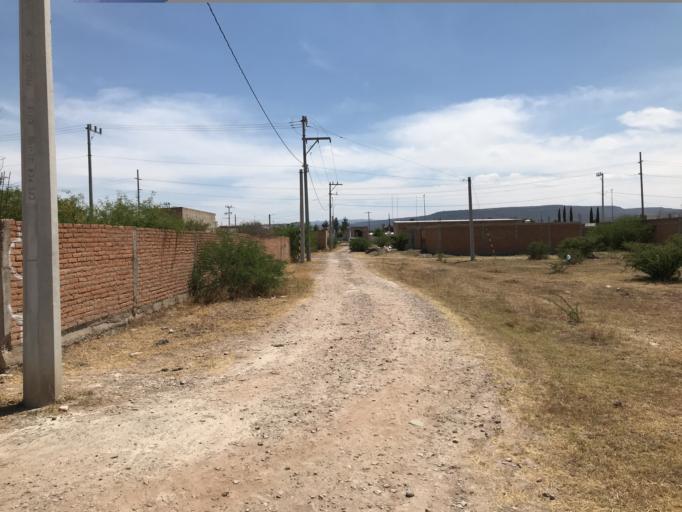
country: MX
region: Durango
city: Victoria de Durango
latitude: 23.9795
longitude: -104.6826
